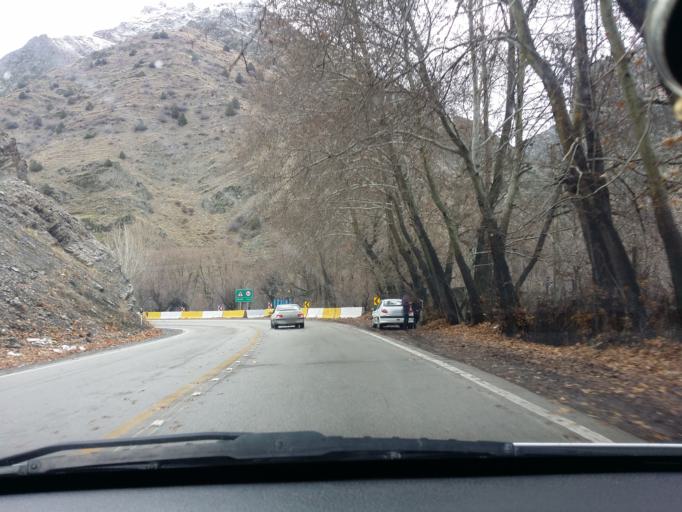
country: IR
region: Tehran
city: Tajrish
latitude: 36.0250
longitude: 51.2479
